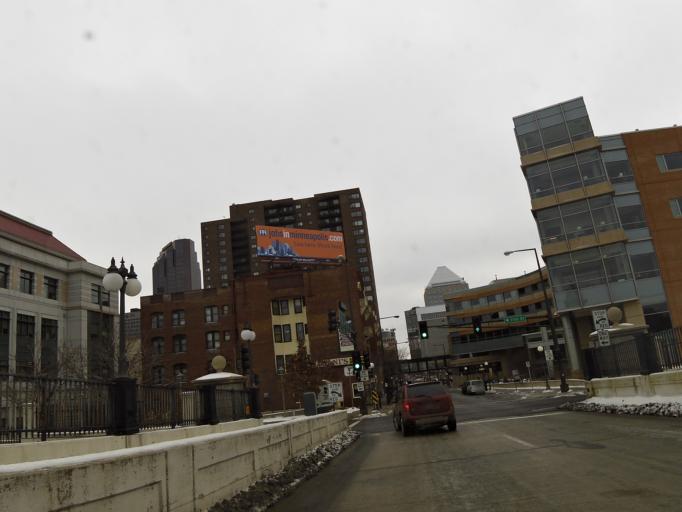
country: US
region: Minnesota
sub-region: Ramsey County
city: Saint Paul
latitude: 44.9502
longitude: -93.1005
